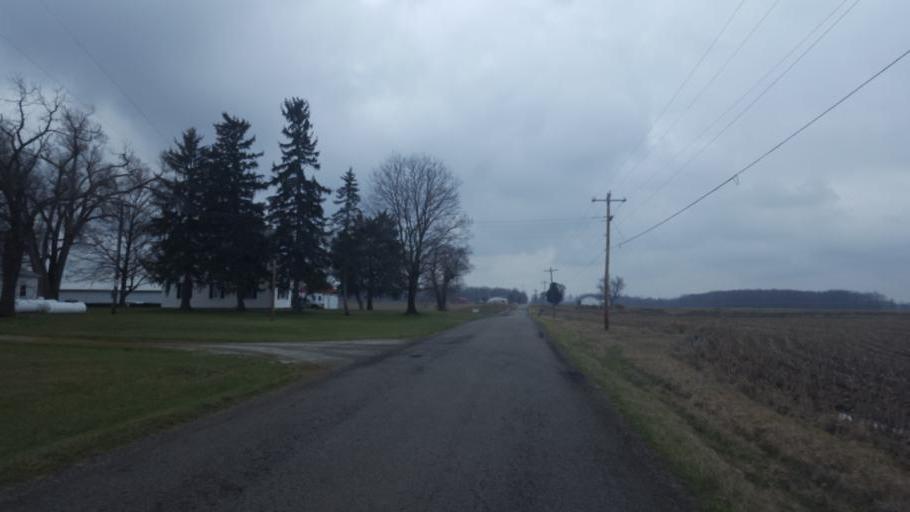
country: US
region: Ohio
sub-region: Delaware County
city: Ashley
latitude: 40.3773
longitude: -82.8537
